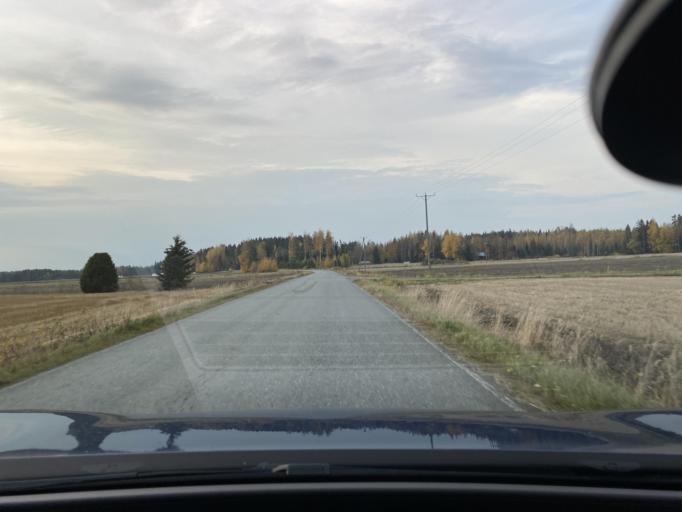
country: FI
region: Pirkanmaa
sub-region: Lounais-Pirkanmaa
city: Punkalaidun
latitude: 61.0783
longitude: 22.9579
